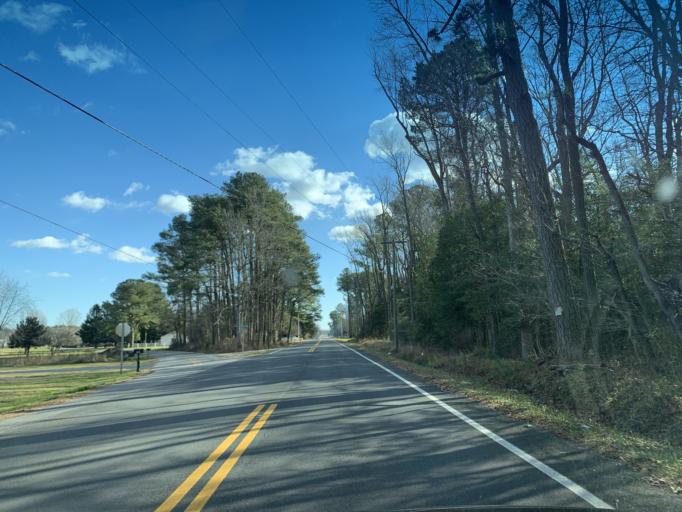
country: US
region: Maryland
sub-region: Worcester County
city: Berlin
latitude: 38.3610
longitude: -75.2000
